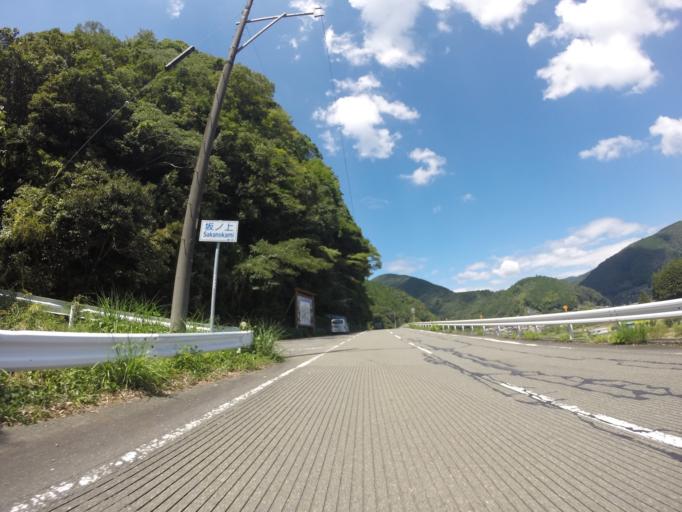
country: JP
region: Shizuoka
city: Shizuoka-shi
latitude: 35.0650
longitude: 138.2437
